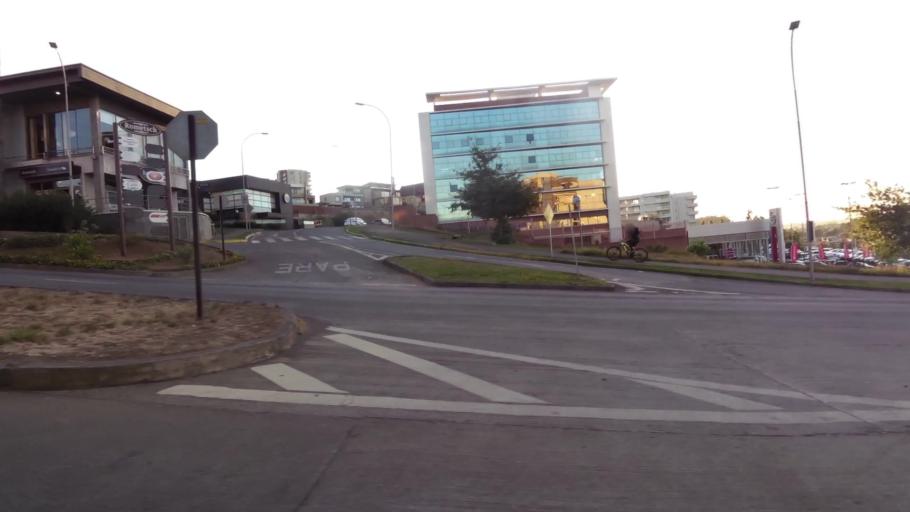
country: CL
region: Biobio
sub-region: Provincia de Concepcion
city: Concepcion
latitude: -36.8466
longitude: -73.0931
